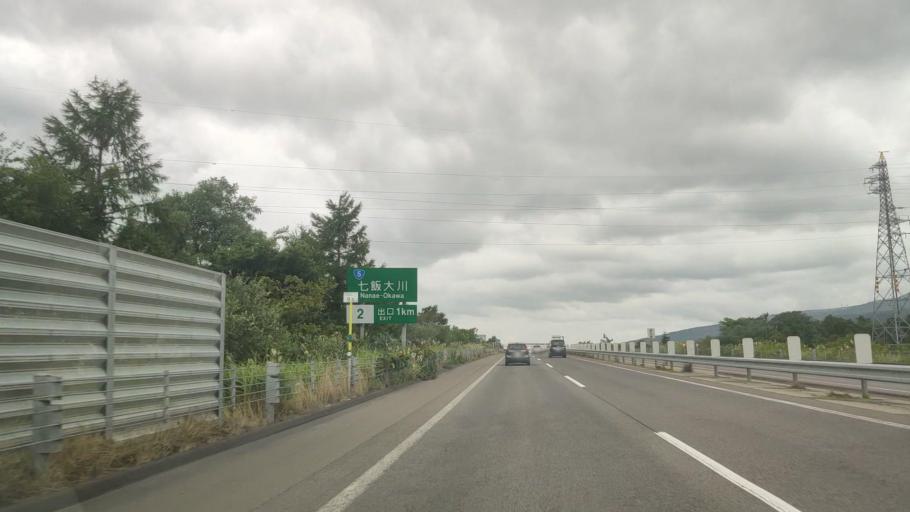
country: JP
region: Hokkaido
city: Nanae
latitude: 41.8580
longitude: 140.7360
